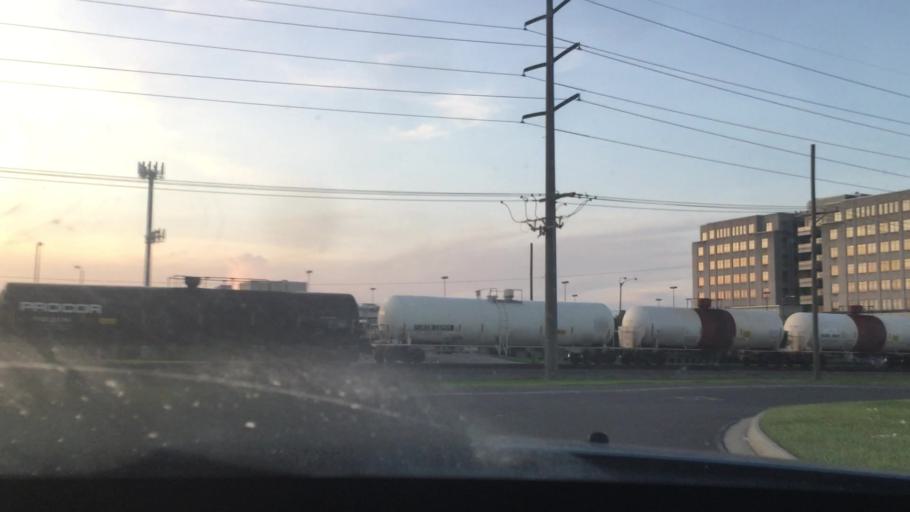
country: US
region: Louisiana
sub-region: West Baton Rouge Parish
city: Port Allen
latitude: 30.4620
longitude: -91.1902
